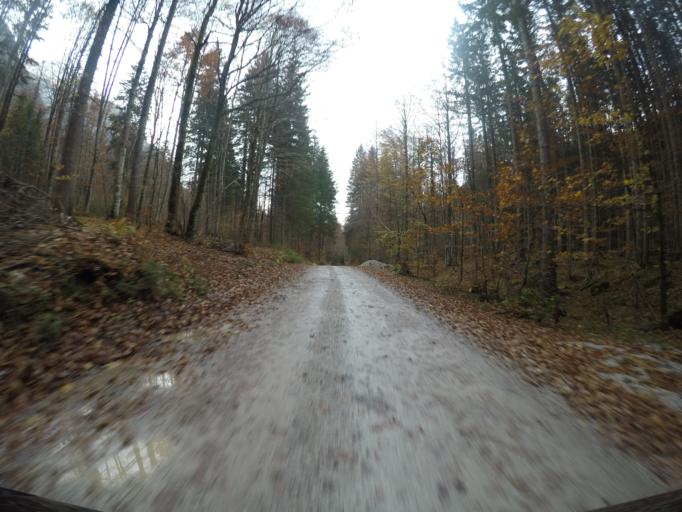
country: SI
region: Kranjska Gora
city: Mojstrana
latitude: 46.4147
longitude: 13.8487
